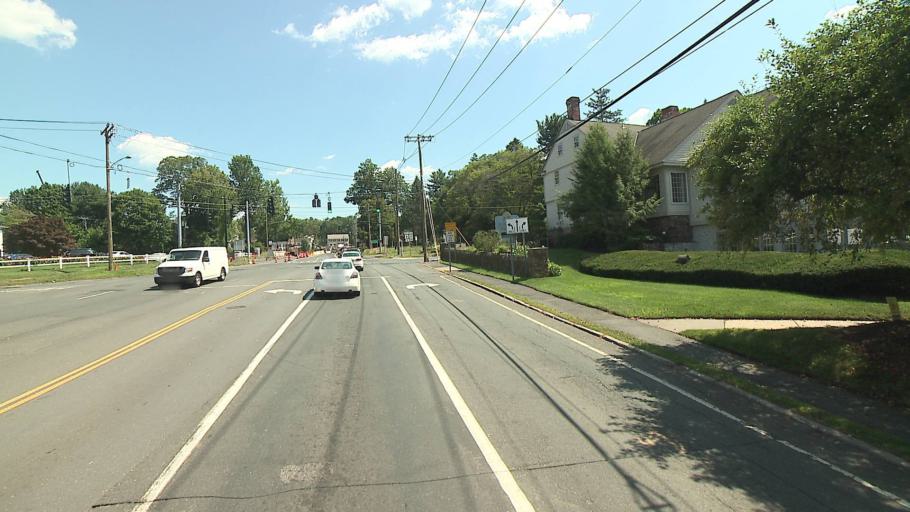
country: US
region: Connecticut
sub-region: Hartford County
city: Farmington
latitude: 41.7267
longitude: -72.8255
